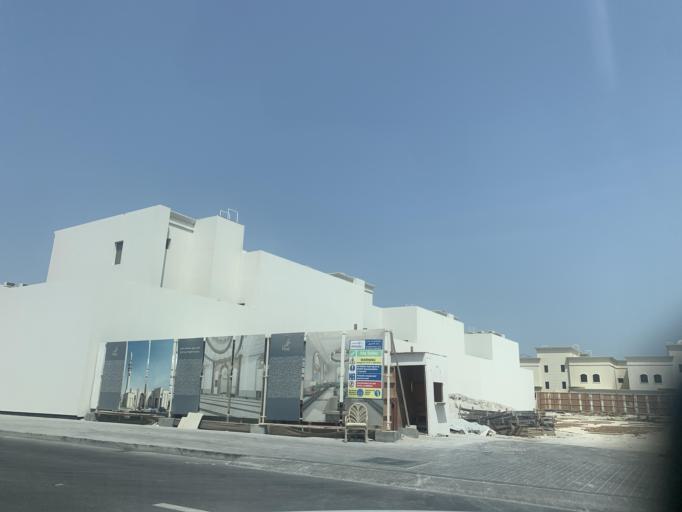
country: BH
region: Muharraq
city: Al Muharraq
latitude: 26.3039
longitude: 50.6301
